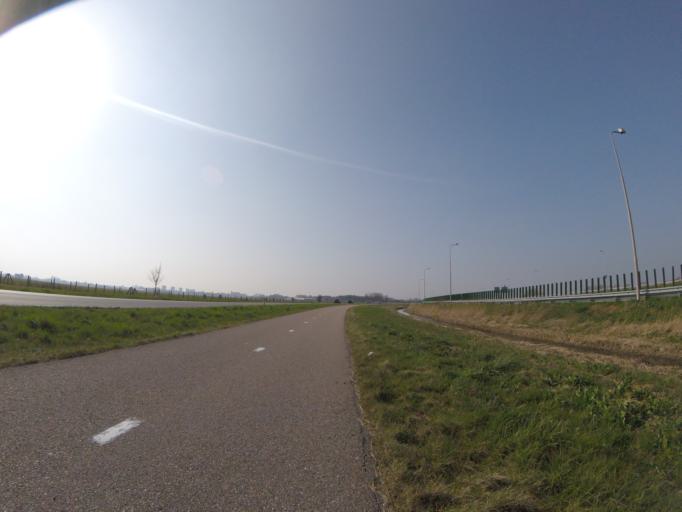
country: NL
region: North Holland
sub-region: Gemeente Haarlem
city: Haarlem
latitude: 52.3695
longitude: 4.6946
